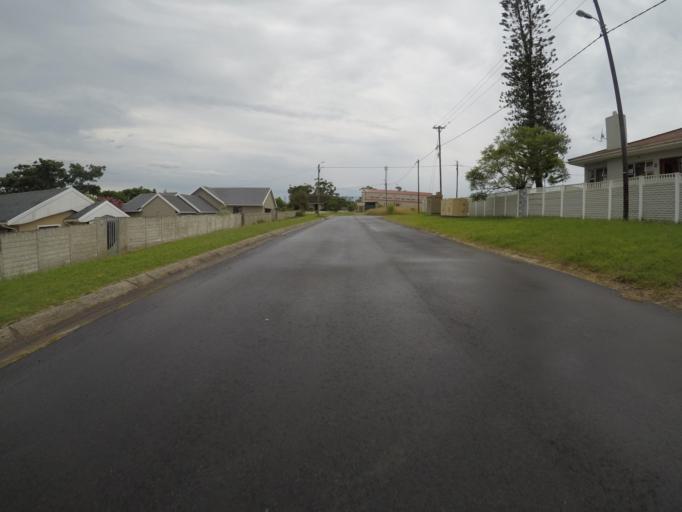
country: ZA
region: Eastern Cape
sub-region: Buffalo City Metropolitan Municipality
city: East London
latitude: -32.9665
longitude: 27.8473
